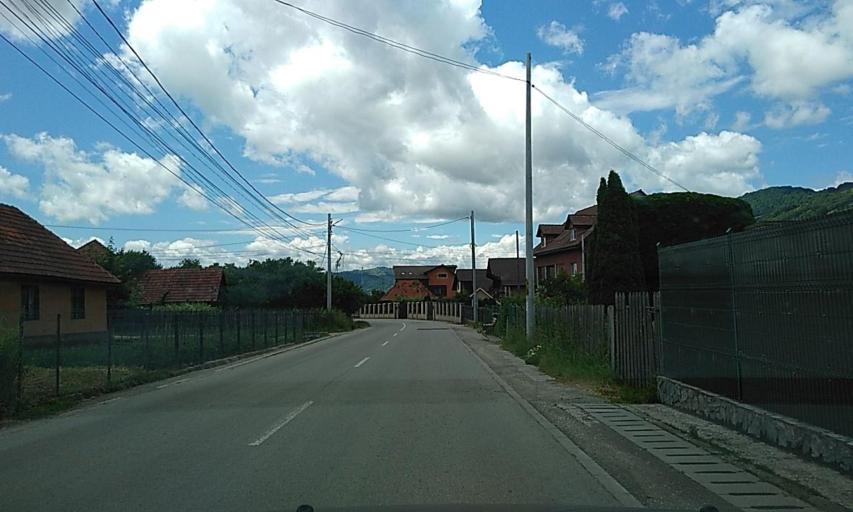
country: RO
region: Hunedoara
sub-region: Oras Petrila
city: Petrila
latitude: 45.4521
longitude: 23.4335
